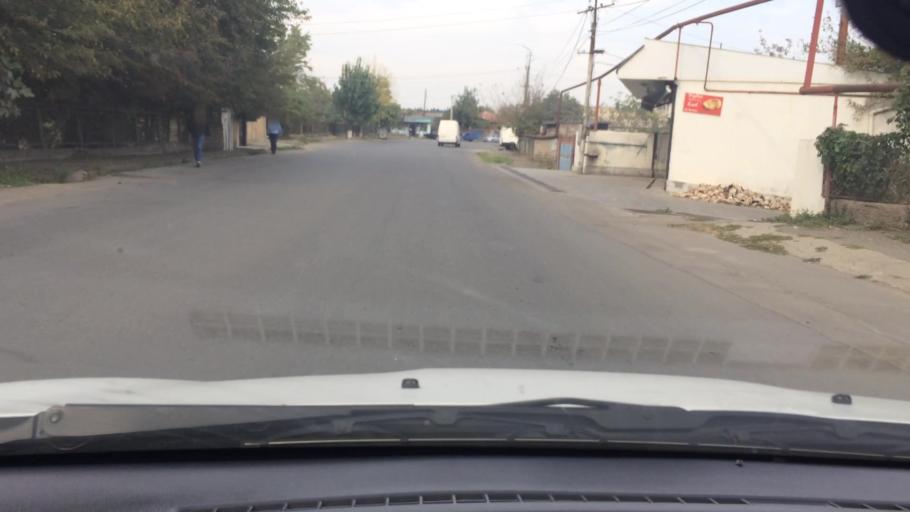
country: GE
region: Kvemo Kartli
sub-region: Marneuli
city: Marneuli
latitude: 41.4623
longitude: 44.8114
